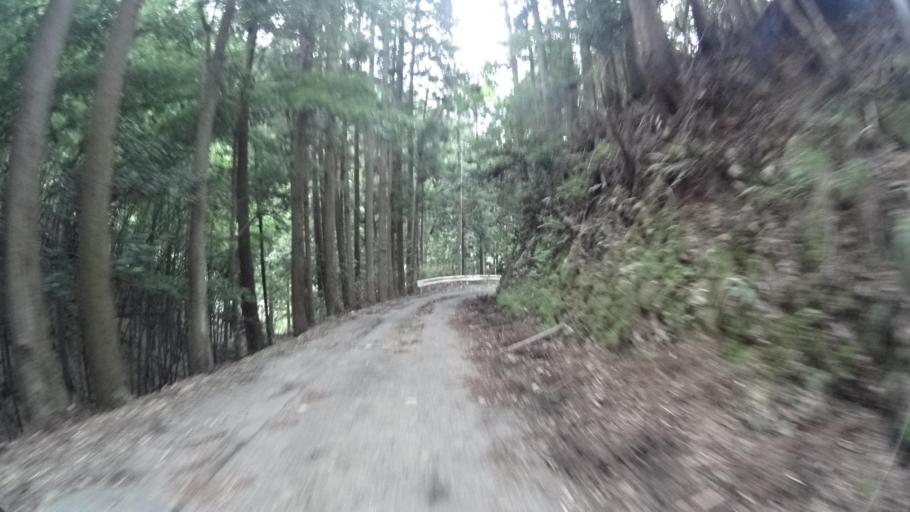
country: JP
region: Kyoto
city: Miyazu
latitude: 35.4357
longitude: 135.1511
